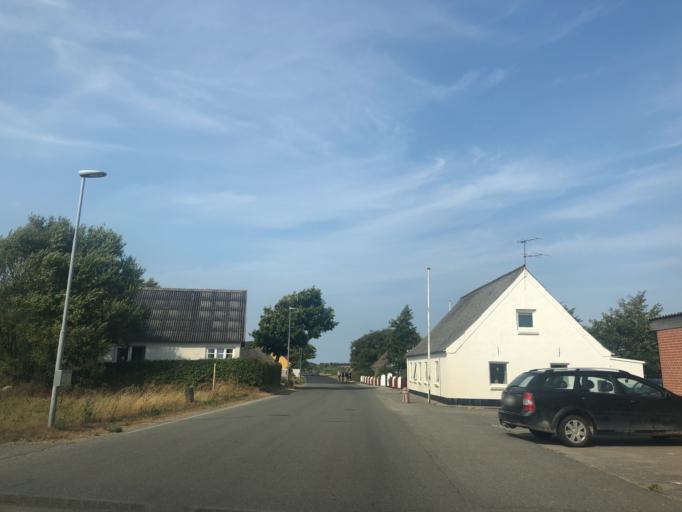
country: DK
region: North Denmark
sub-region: Morso Kommune
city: Nykobing Mors
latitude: 56.8197
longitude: 9.0297
